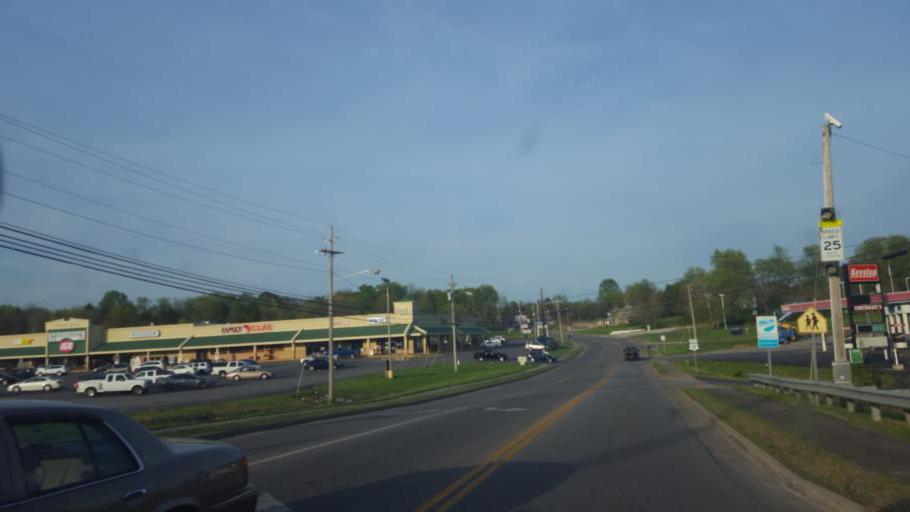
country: US
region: Kentucky
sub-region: Barren County
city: Glasgow
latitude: 36.9828
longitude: -85.9311
